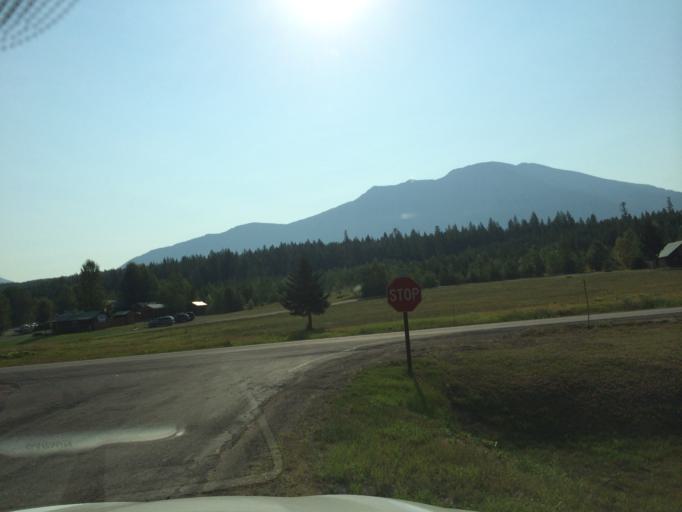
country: US
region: Montana
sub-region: Flathead County
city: Columbia Falls
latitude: 48.4816
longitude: -114.0023
